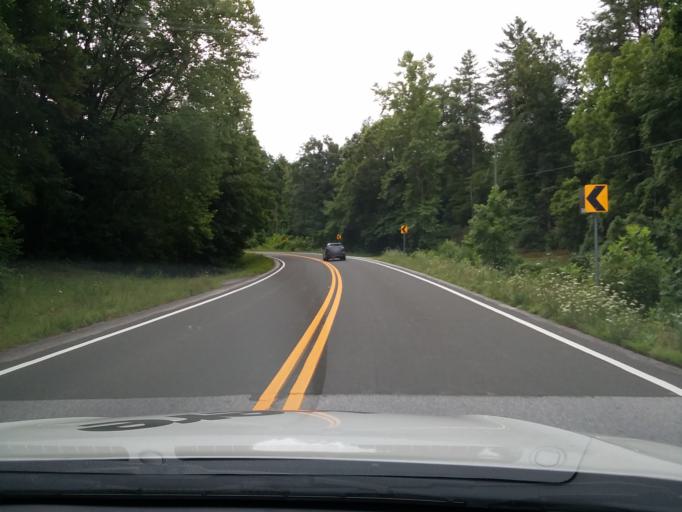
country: US
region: Georgia
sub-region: Rabun County
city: Clayton
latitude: 34.8358
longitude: -83.3309
